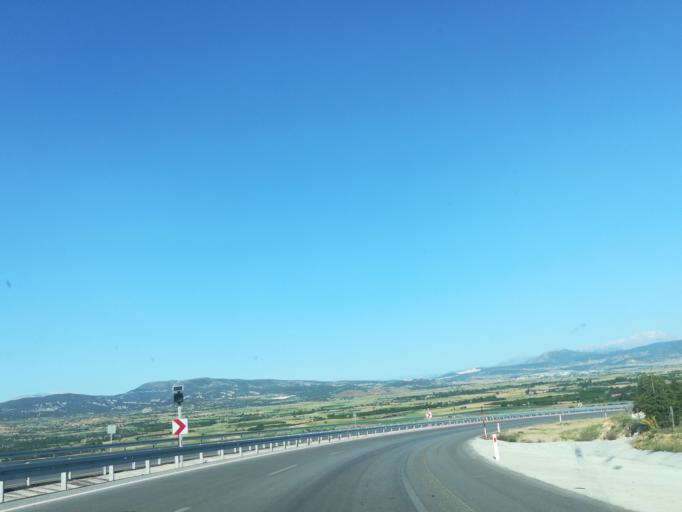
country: TR
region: Isparta
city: Keciborlu
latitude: 37.9190
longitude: 30.2958
